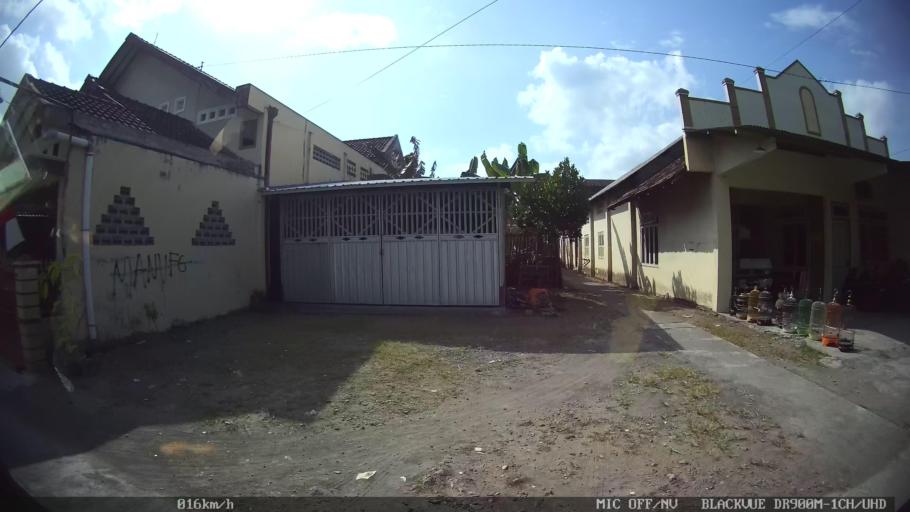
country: ID
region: Daerah Istimewa Yogyakarta
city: Kasihan
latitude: -7.8336
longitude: 110.3639
